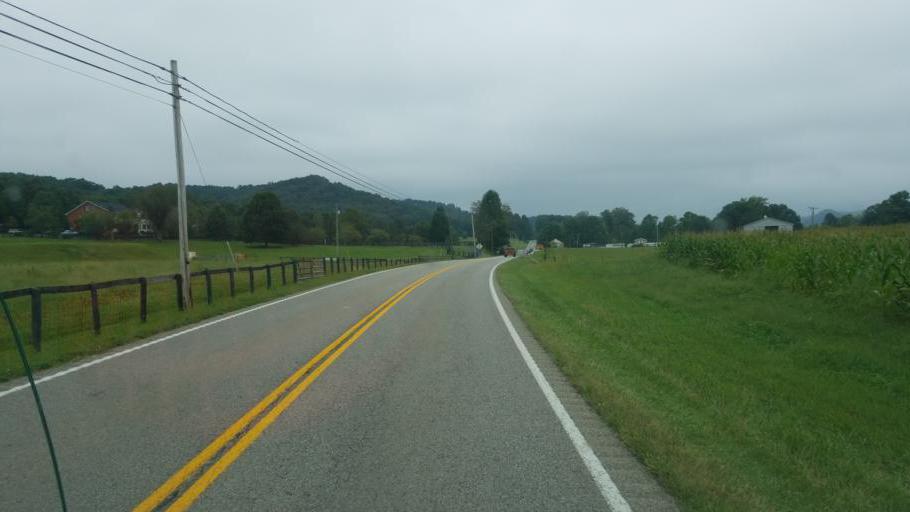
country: US
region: Kentucky
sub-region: Rowan County
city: Morehead
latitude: 38.2186
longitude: -83.4714
